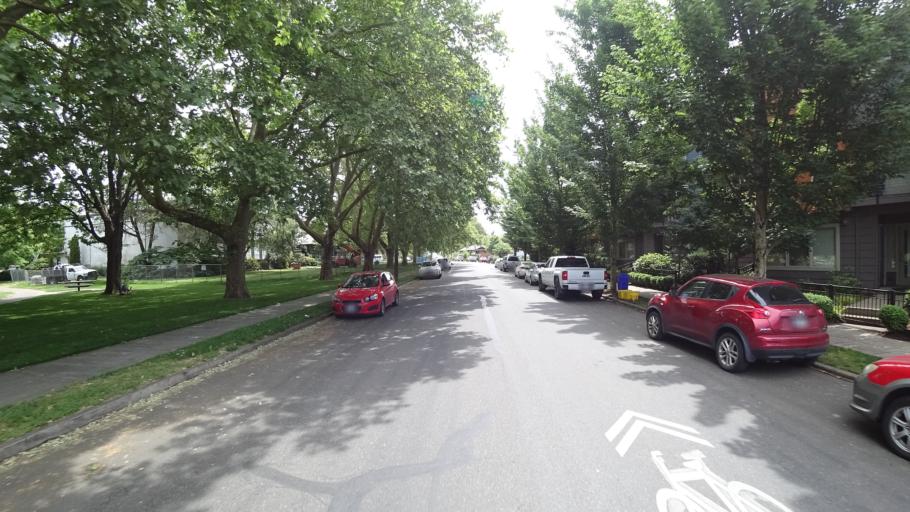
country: US
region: Oregon
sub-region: Washington County
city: West Haven
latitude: 45.5923
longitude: -122.7531
